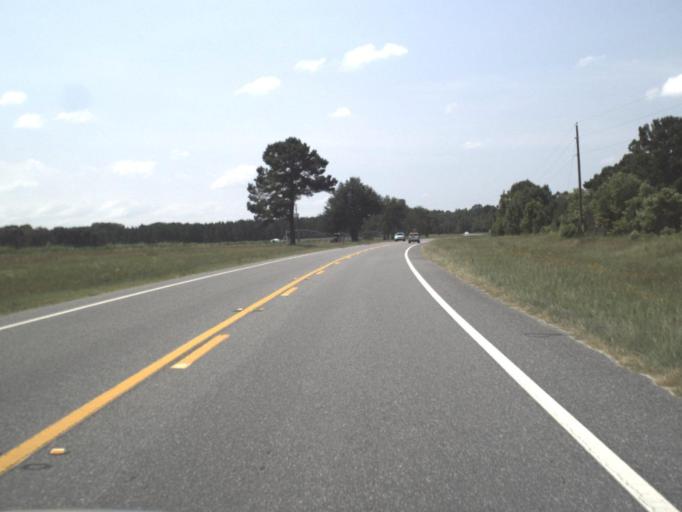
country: US
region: Georgia
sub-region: Echols County
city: Statenville
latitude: 30.5948
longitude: -83.0941
